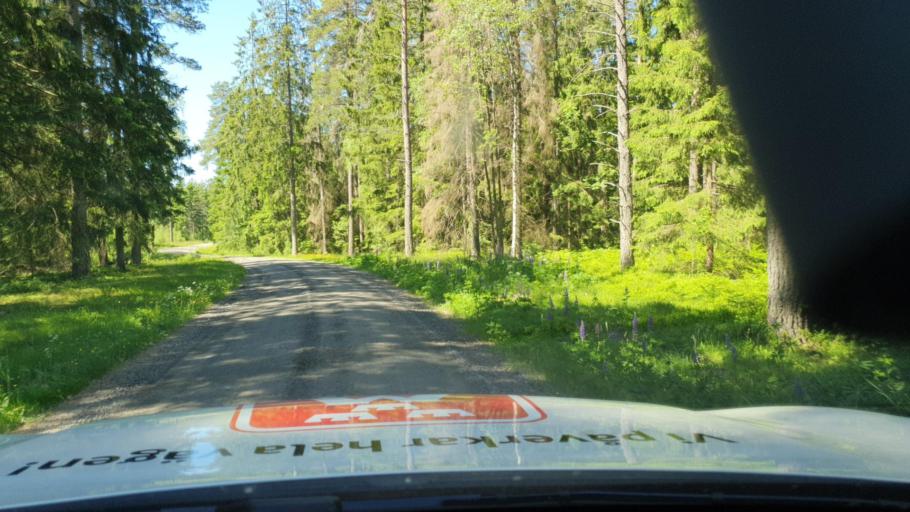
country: SE
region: Joenkoeping
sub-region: Mullsjo Kommun
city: Mullsjoe
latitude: 57.8925
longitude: 13.9391
